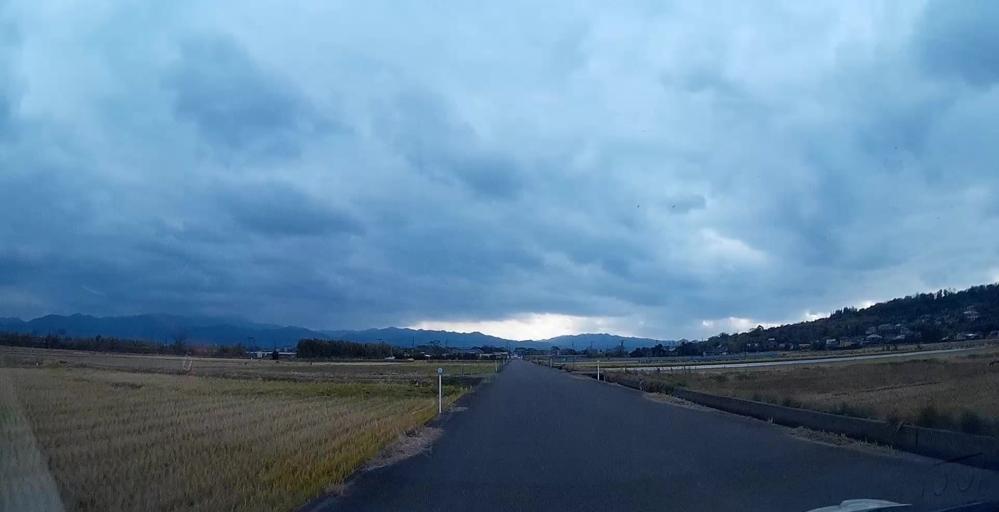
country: JP
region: Kagoshima
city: Izumi
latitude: 32.0988
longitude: 130.2753
